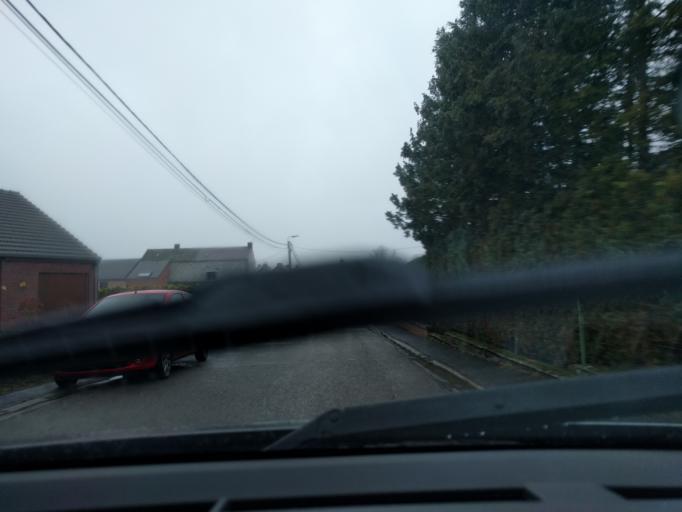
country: BE
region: Wallonia
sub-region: Province de Namur
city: Couvin
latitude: 50.0487
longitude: 4.5035
